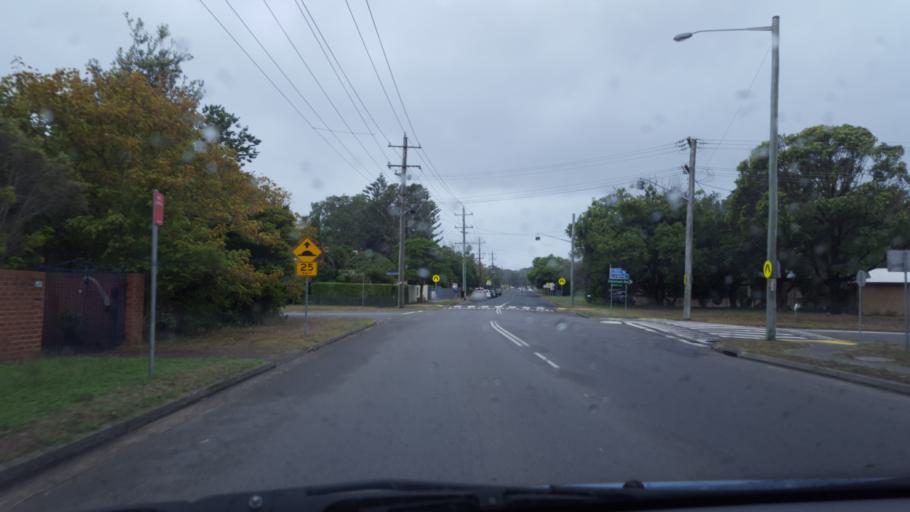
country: AU
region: New South Wales
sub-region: Port Stephens Shire
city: Anna Bay
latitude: -32.7775
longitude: 152.0857
